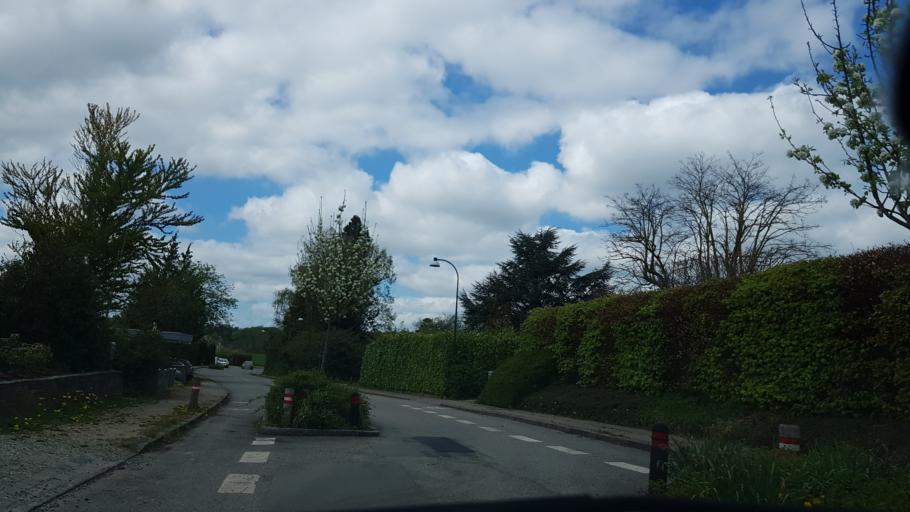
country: DK
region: Capital Region
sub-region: Rudersdal Kommune
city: Trorod
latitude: 55.8464
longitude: 12.5405
